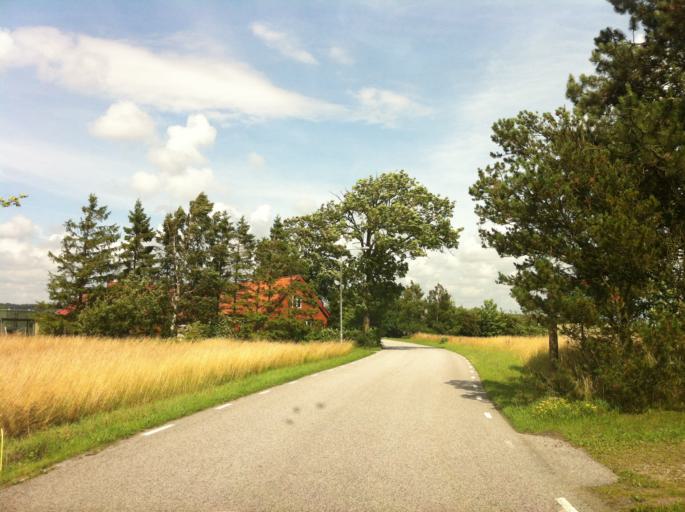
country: SE
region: Skane
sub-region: Skurups Kommun
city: Skurup
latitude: 55.4576
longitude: 13.4289
